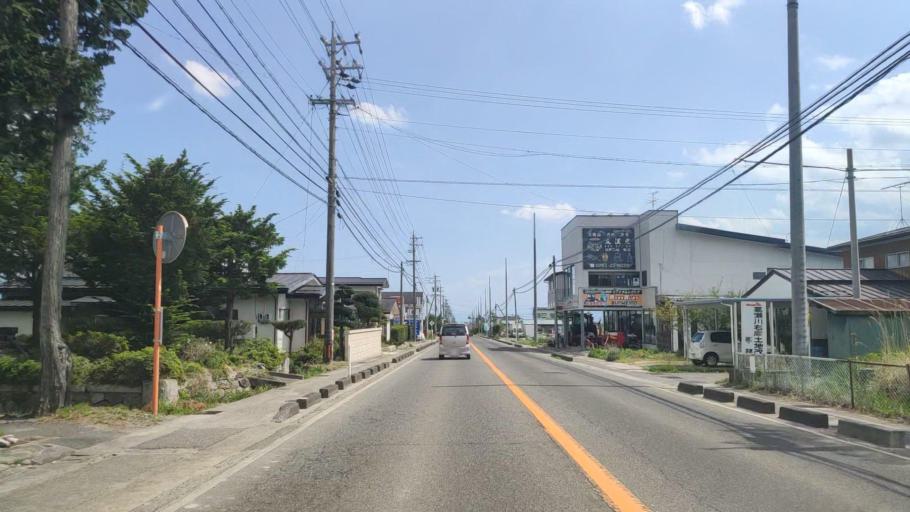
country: JP
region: Nagano
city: Omachi
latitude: 36.4640
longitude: 137.8497
